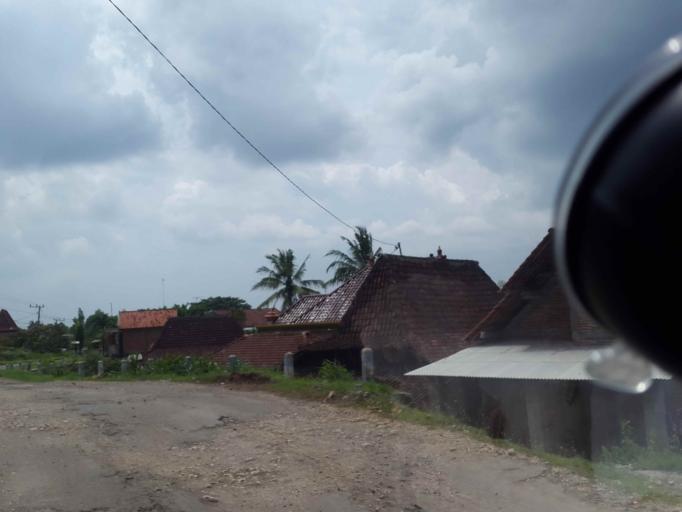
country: ID
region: East Java
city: Ruser
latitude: -8.2117
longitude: 112.0202
